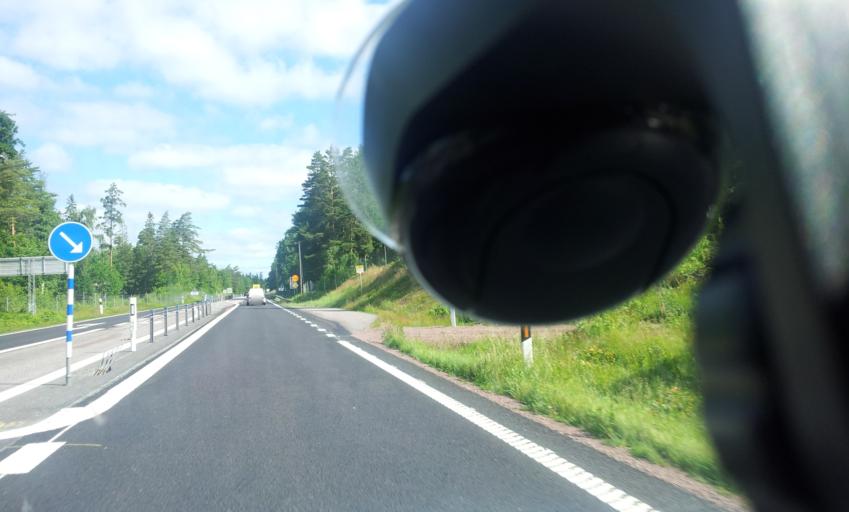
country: SE
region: Kalmar
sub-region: Monsteras Kommun
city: Timmernabben
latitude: 56.8944
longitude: 16.3804
